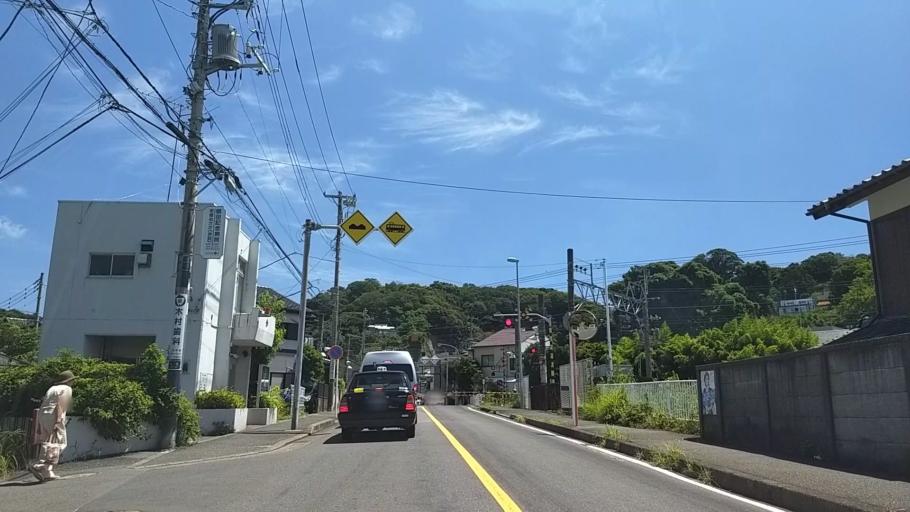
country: JP
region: Kanagawa
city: Kamakura
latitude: 35.3109
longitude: 139.5577
